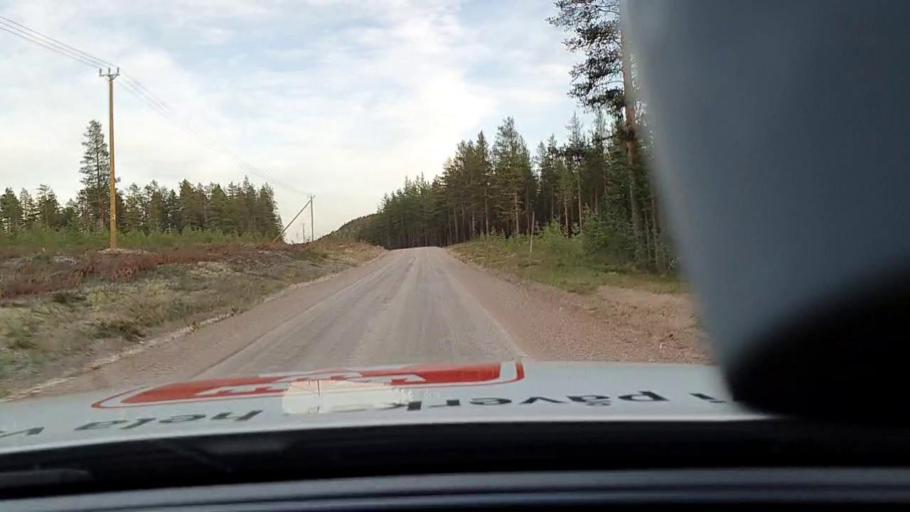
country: SE
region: Norrbotten
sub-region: Overkalix Kommun
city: OEverkalix
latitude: 66.3284
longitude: 22.5923
